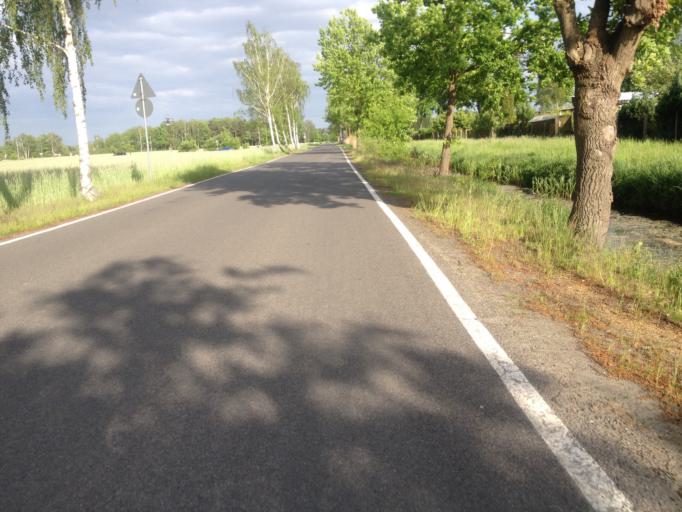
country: DE
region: Brandenburg
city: Cottbus
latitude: 51.8136
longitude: 14.3309
